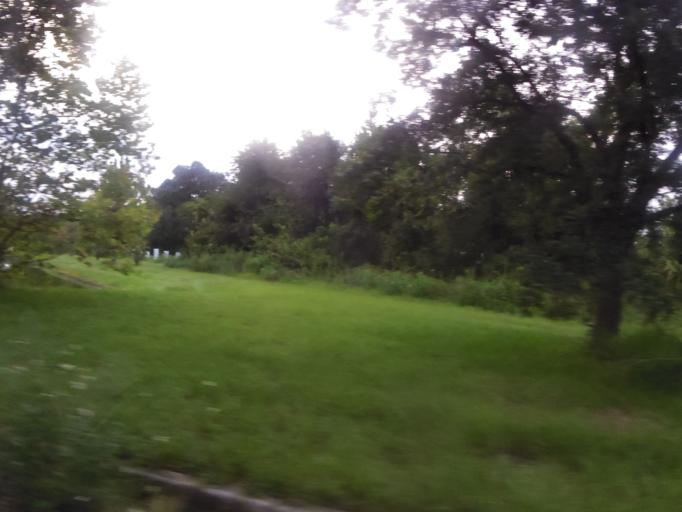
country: US
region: Florida
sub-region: Duval County
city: Jacksonville
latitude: 30.3478
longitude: -81.6972
